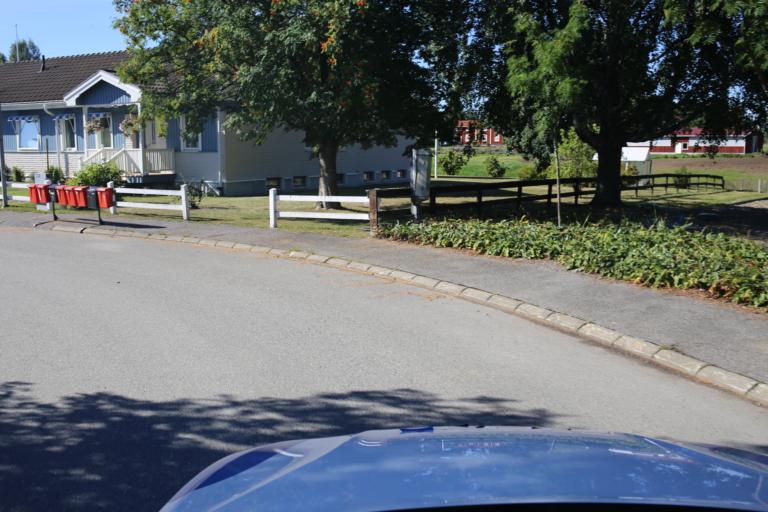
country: SE
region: Vaesterbotten
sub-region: Skelleftea Kommun
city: Viken
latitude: 64.7460
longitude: 20.7659
